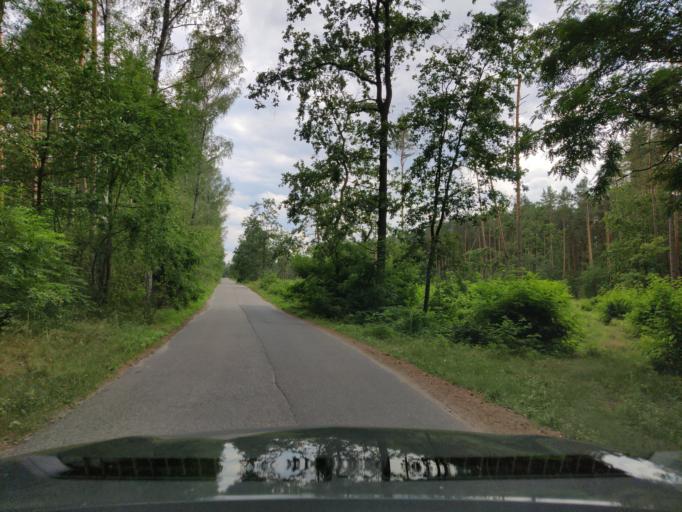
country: PL
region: Masovian Voivodeship
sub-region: Powiat pultuski
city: Pultusk
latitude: 52.7353
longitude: 21.1370
